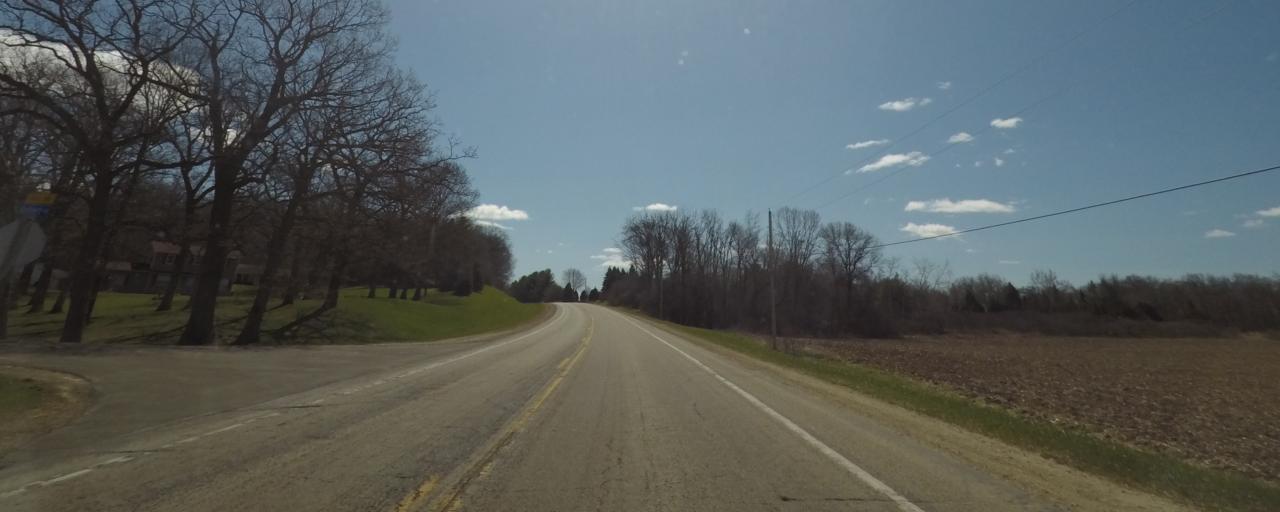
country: US
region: Wisconsin
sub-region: Dane County
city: Cottage Grove
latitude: 43.0837
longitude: -89.1621
